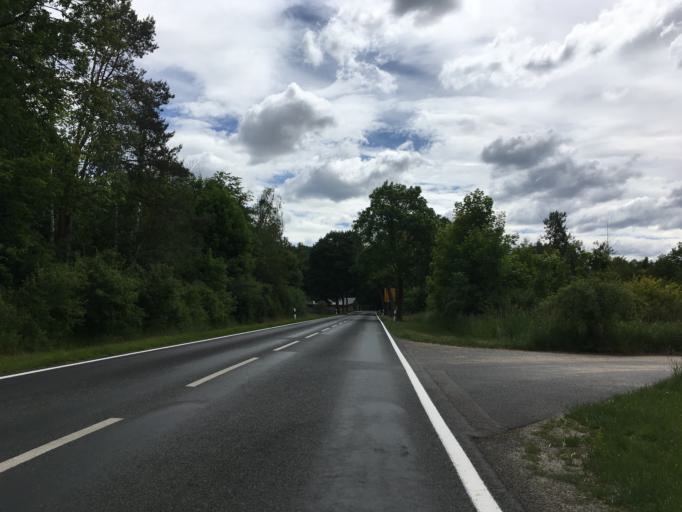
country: DE
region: Brandenburg
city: Melchow
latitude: 52.7514
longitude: 13.6827
